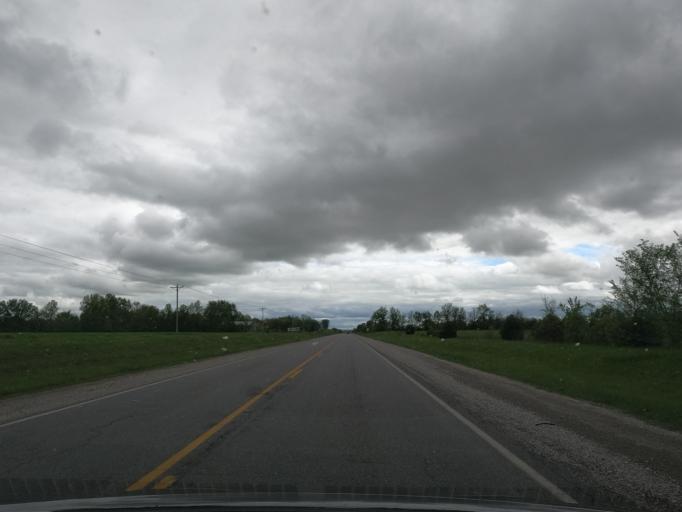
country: US
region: Missouri
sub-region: Jasper County
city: Oronogo
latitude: 37.3300
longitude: -94.4849
